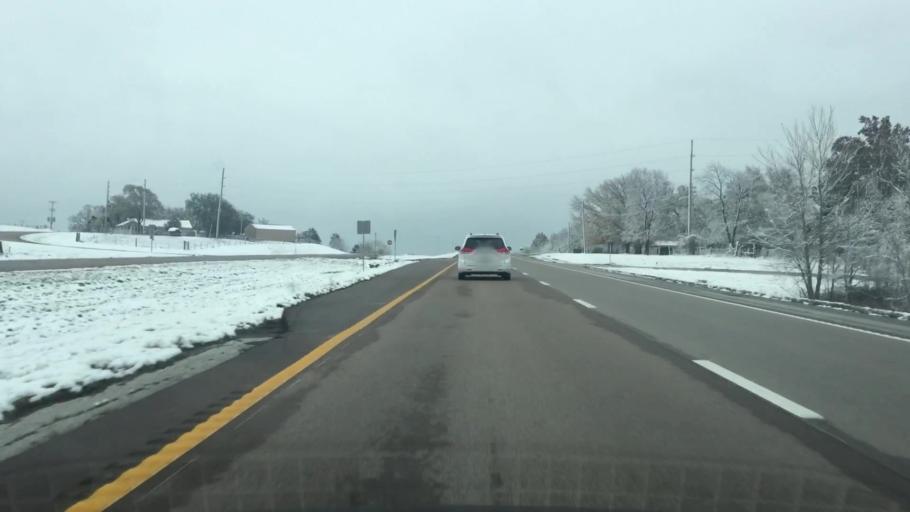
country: US
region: Missouri
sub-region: Cass County
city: Garden City
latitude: 38.4926
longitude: -94.0558
